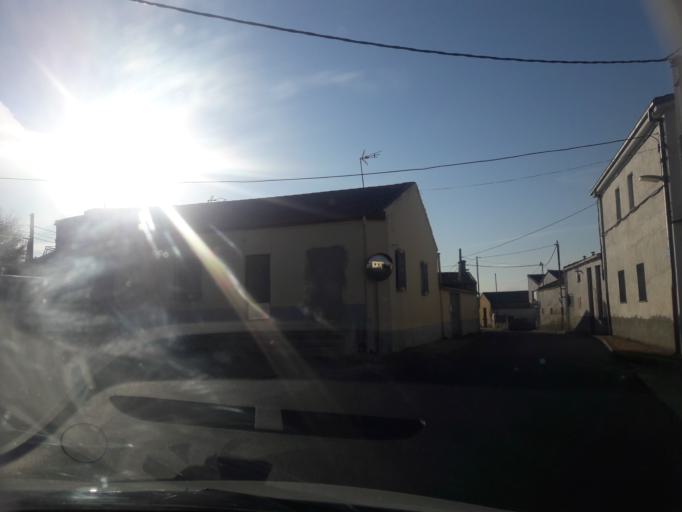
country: ES
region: Castille and Leon
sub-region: Provincia de Salamanca
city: Montejo
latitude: 40.6319
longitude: -5.6230
